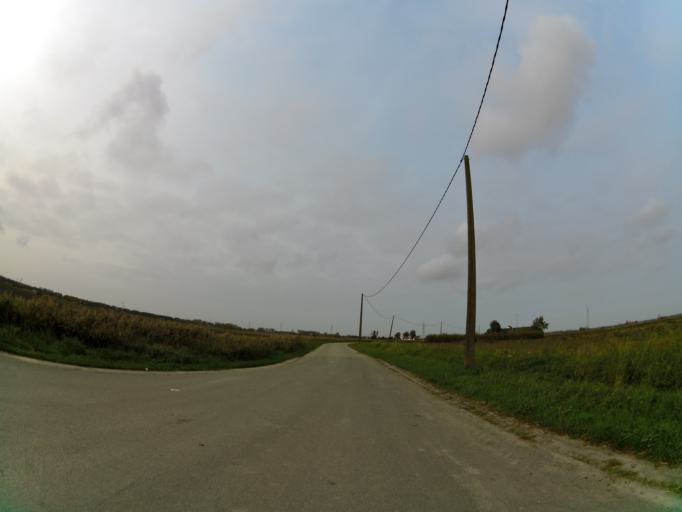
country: BE
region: Flanders
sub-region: Provincie West-Vlaanderen
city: Oudenburg
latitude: 51.2193
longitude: 3.0126
